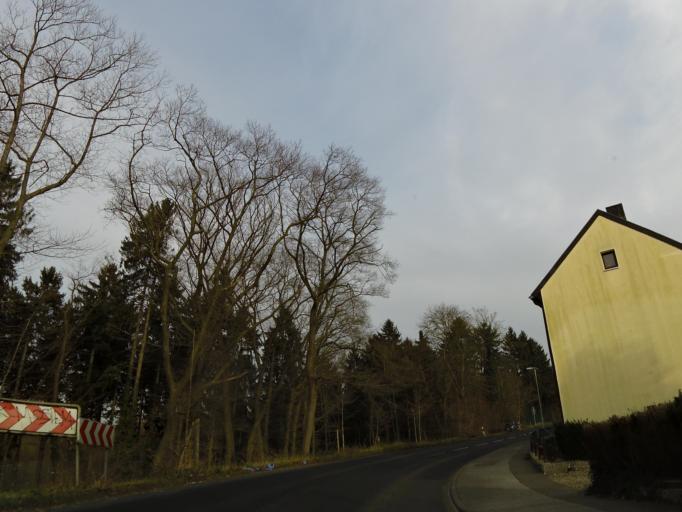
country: DE
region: North Rhine-Westphalia
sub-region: Regierungsbezirk Koln
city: Herzogenrath
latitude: 50.8437
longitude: 6.0986
